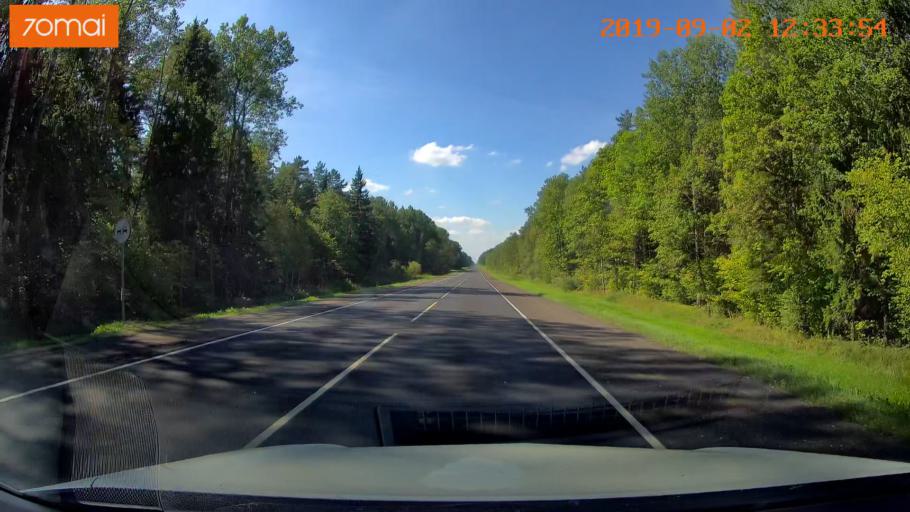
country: RU
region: Smolensk
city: Shumyachi
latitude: 53.8144
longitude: 32.4175
